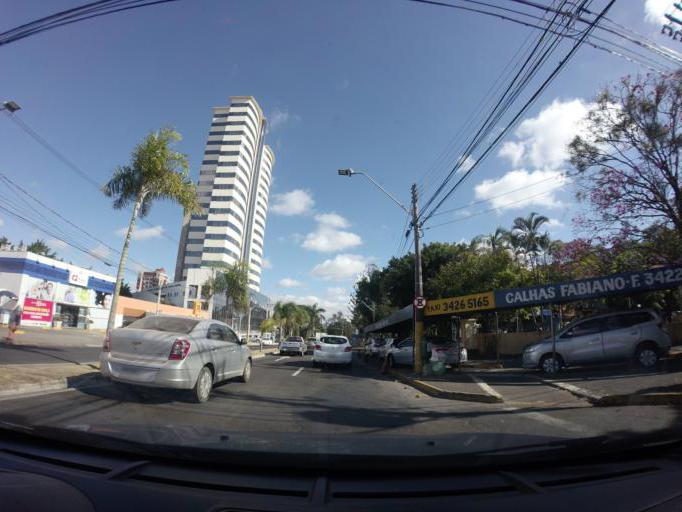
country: BR
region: Sao Paulo
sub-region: Piracicaba
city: Piracicaba
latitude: -22.7380
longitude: -47.6428
